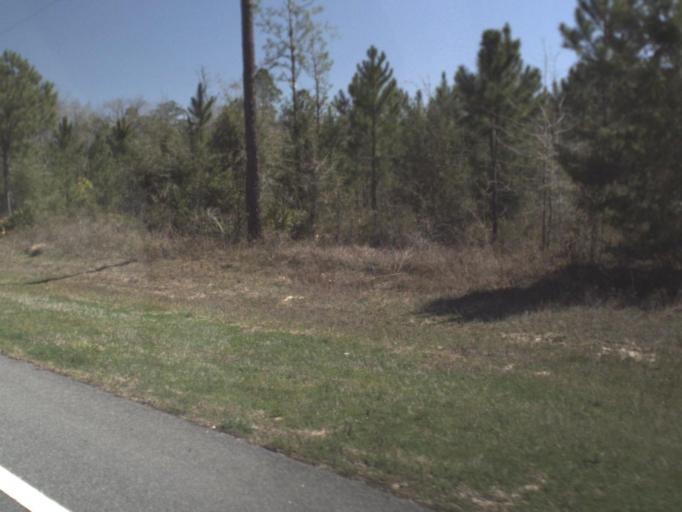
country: US
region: Florida
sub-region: Gadsden County
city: Quincy
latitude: 30.4132
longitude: -84.6658
